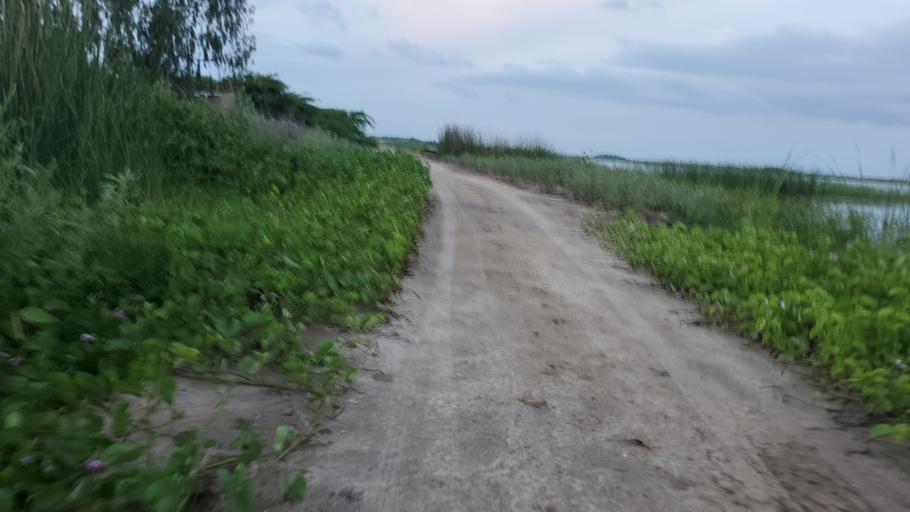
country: SN
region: Saint-Louis
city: Saint-Louis
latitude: 16.0384
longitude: -16.4172
